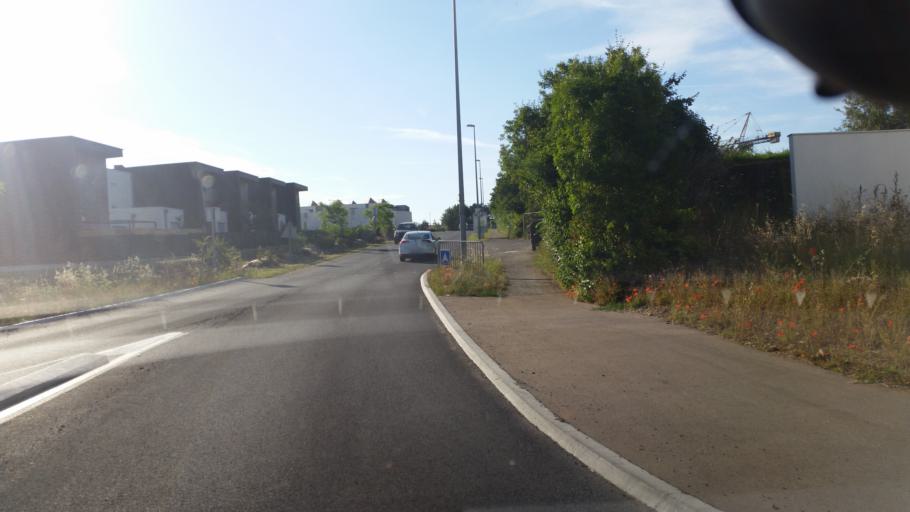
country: FR
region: Poitou-Charentes
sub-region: Departement de la Charente-Maritime
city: Puilboreau
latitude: 46.1726
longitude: -1.1100
